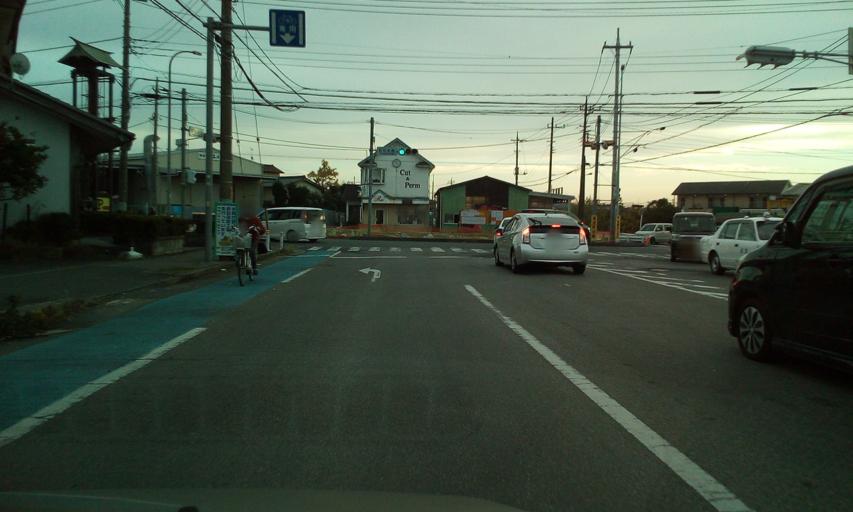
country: JP
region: Saitama
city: Yashio-shi
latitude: 35.8498
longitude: 139.8604
